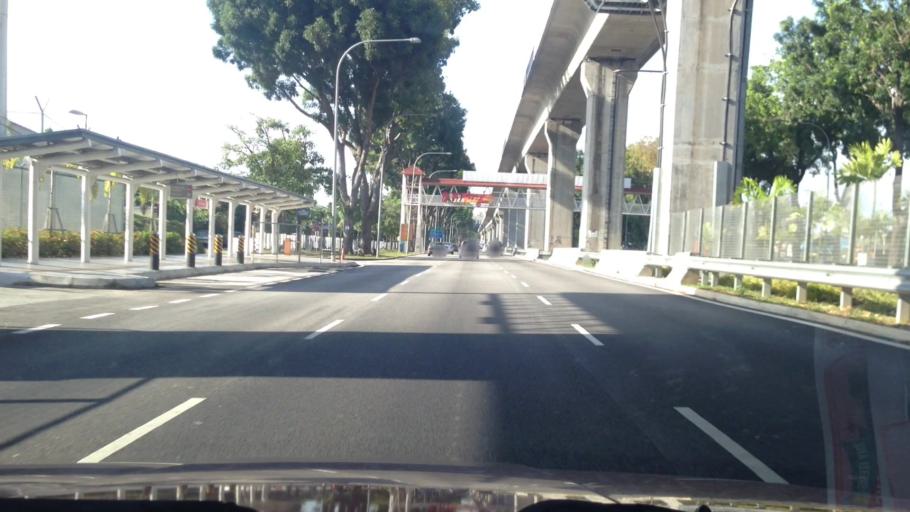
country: MY
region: Selangor
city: Subang Jaya
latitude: 3.0352
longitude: 101.5881
